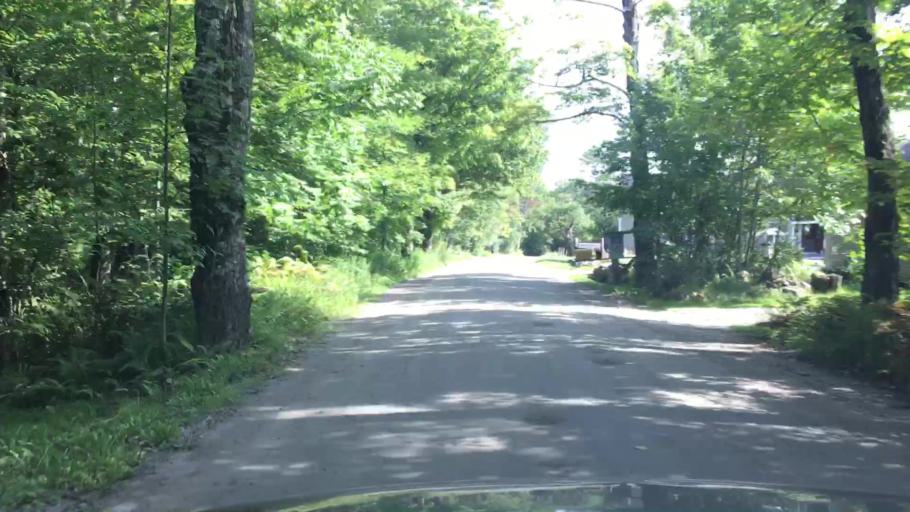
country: US
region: Vermont
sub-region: Windham County
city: Dover
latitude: 42.8279
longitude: -72.7975
